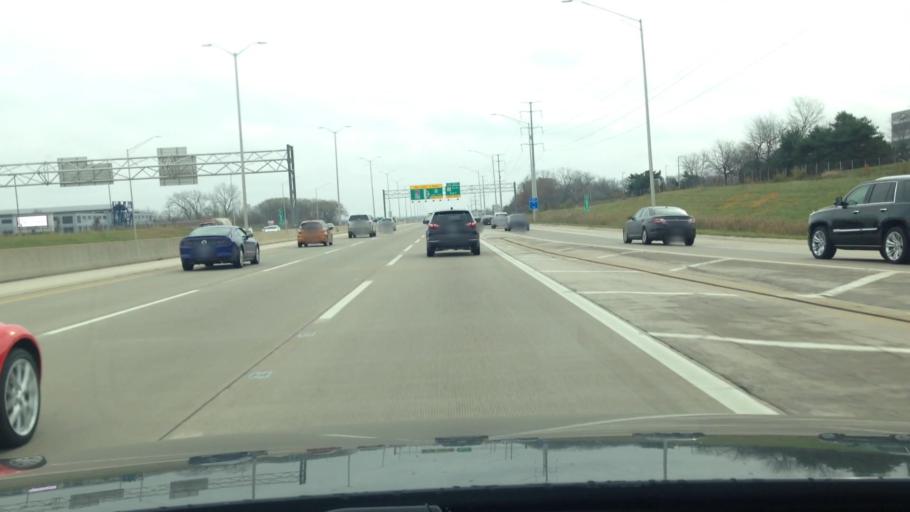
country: US
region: Illinois
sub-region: Kane County
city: Sleepy Hollow
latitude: 42.0786
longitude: -88.3311
